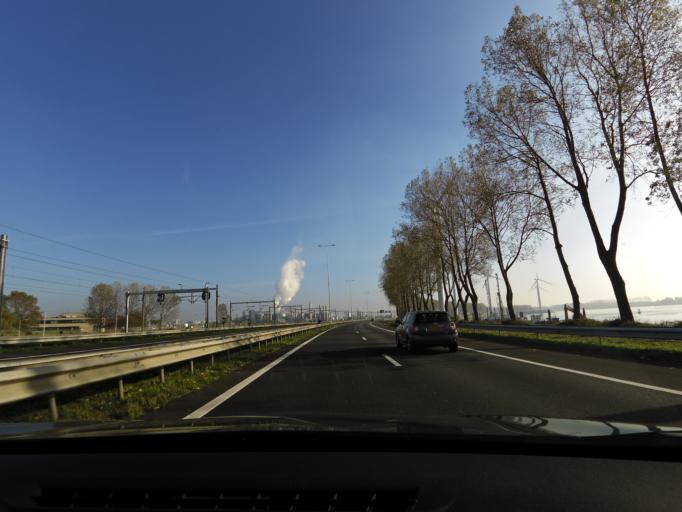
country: NL
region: South Holland
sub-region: Gemeente Brielle
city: Brielle
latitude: 51.9308
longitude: 4.1659
